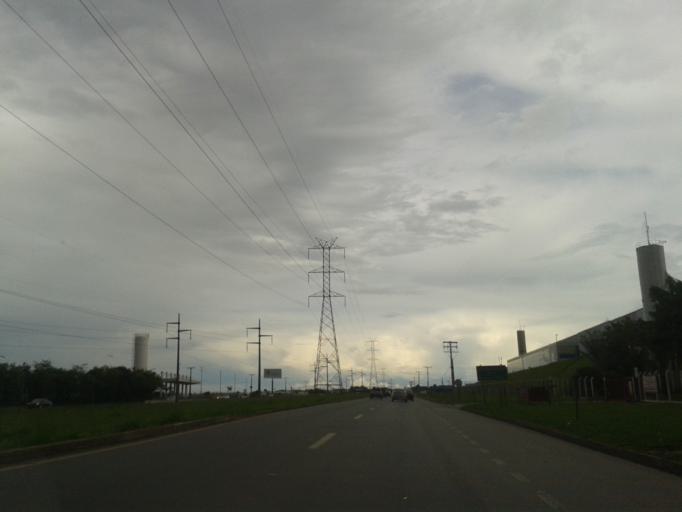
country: BR
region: Goias
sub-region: Aparecida De Goiania
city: Aparecida de Goiania
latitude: -16.7862
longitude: -49.2561
